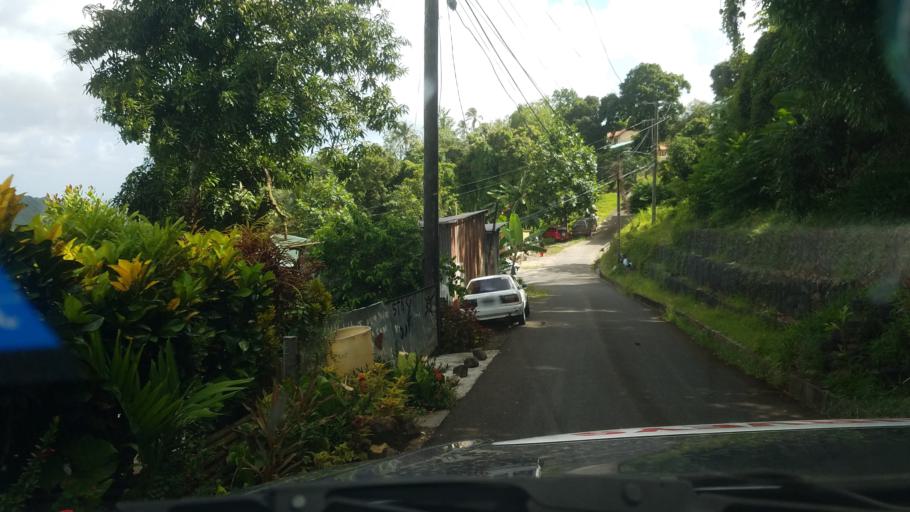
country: LC
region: Castries Quarter
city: Bisee
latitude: 14.0071
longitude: -60.9549
